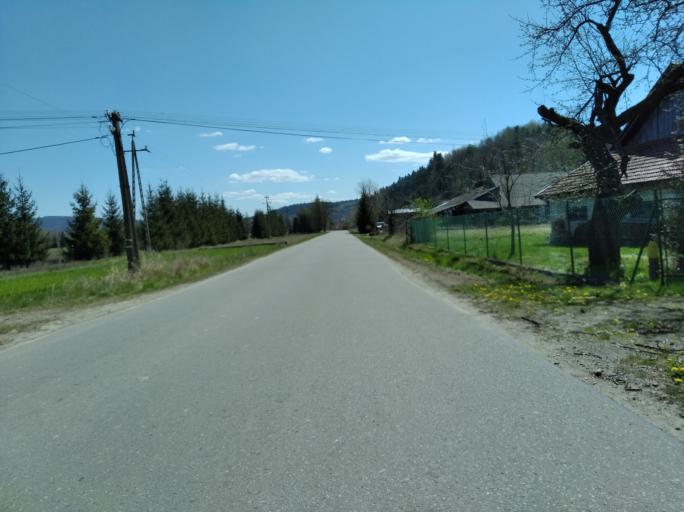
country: PL
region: Subcarpathian Voivodeship
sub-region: Powiat brzozowski
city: Dydnia
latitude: 49.6980
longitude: 22.1931
